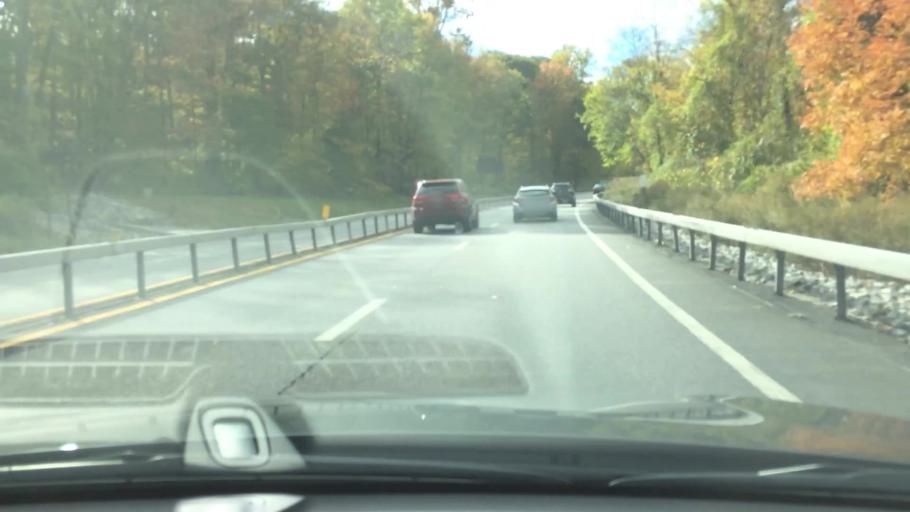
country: US
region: New York
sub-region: Dutchess County
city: Brinckerhoff
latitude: 41.4994
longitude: -73.7965
